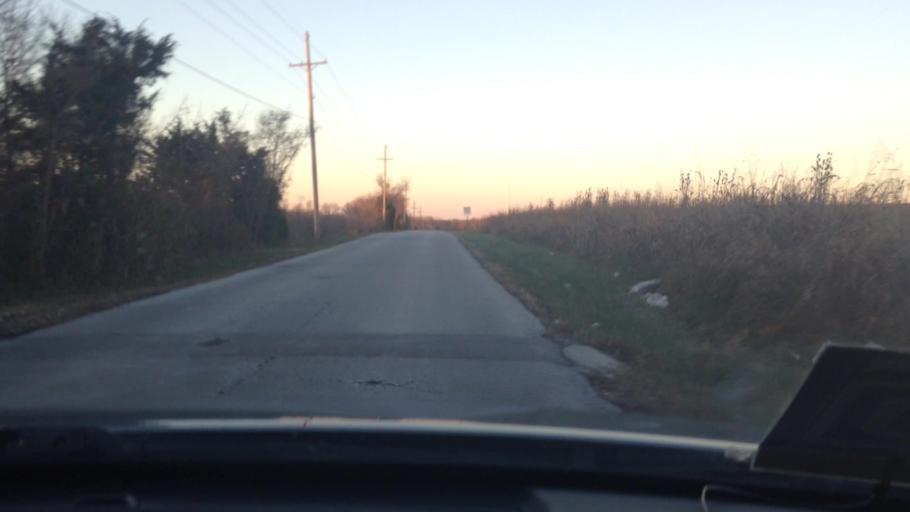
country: US
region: Kansas
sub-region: Wyandotte County
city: Bonner Springs
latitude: 39.1206
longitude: -94.8538
